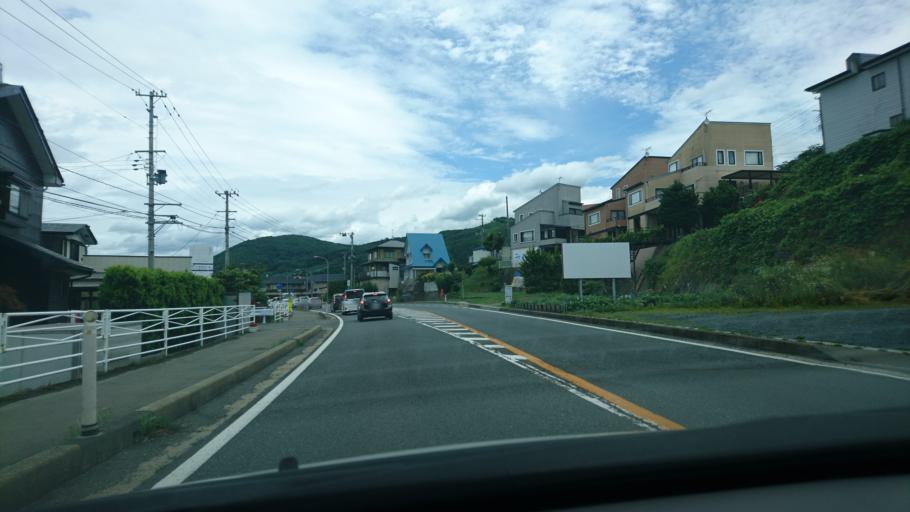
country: JP
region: Iwate
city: Morioka-shi
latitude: 39.6364
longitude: 141.1855
